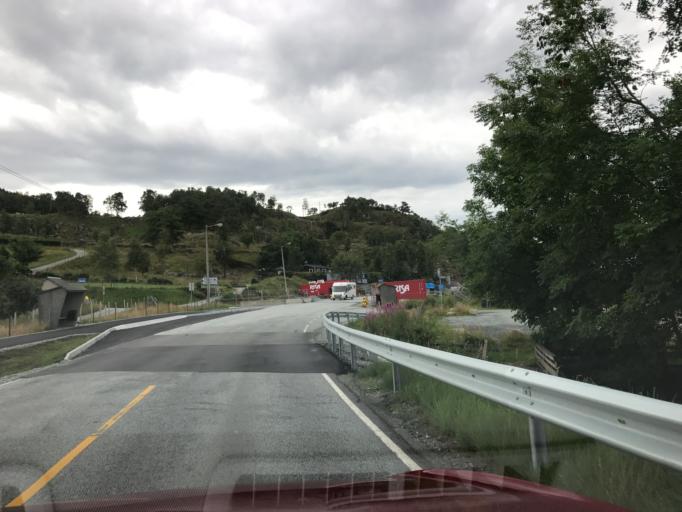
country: NO
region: Rogaland
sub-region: Strand
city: Tau
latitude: 59.0469
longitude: 5.9244
